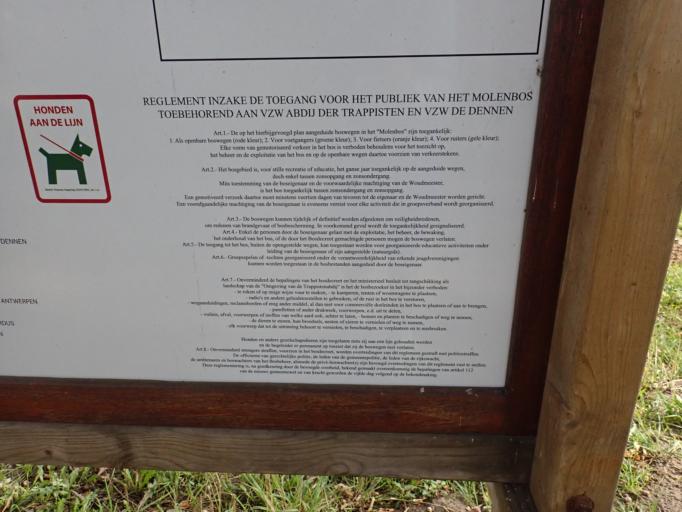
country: BE
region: Flanders
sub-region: Provincie Antwerpen
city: Zoersel
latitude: 51.2851
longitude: 4.6586
